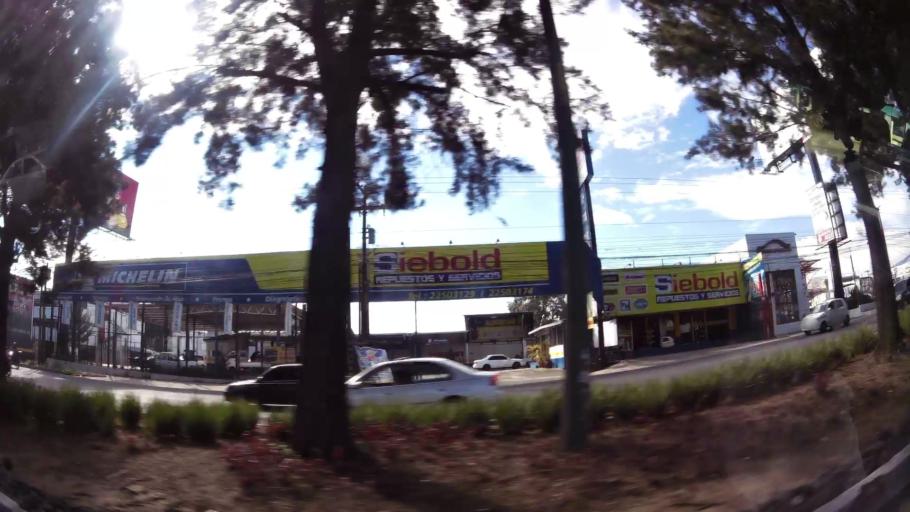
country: GT
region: Guatemala
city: Mixco
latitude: 14.6340
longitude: -90.5778
